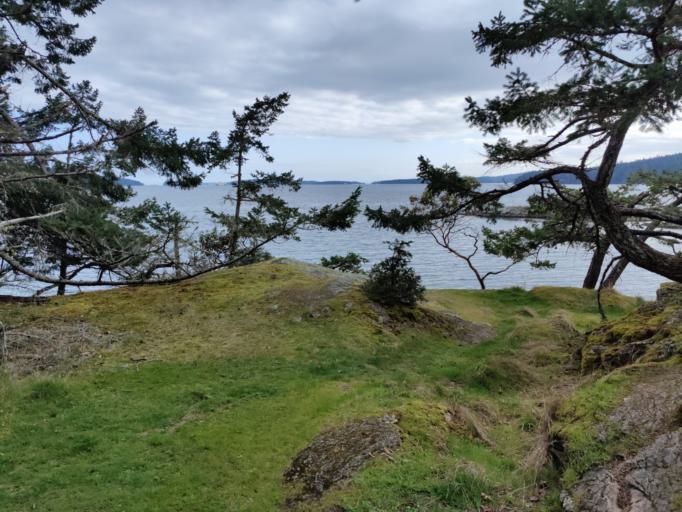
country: CA
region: British Columbia
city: North Saanich
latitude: 48.7561
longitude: -123.4241
